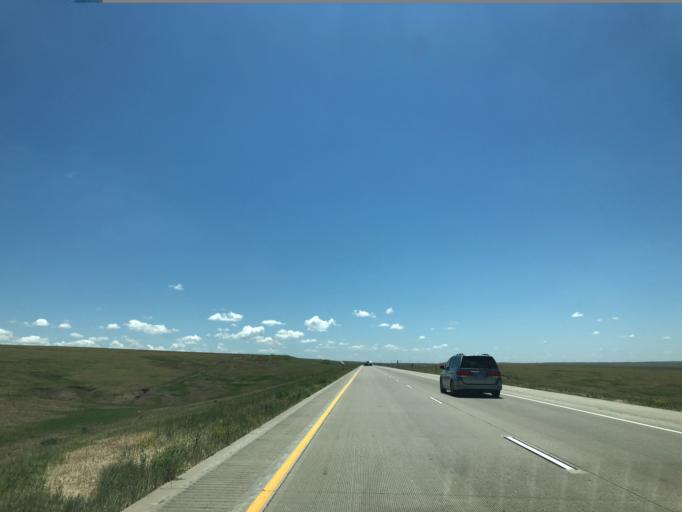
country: US
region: Colorado
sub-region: Lincoln County
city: Limon
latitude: 39.3901
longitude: -103.8935
